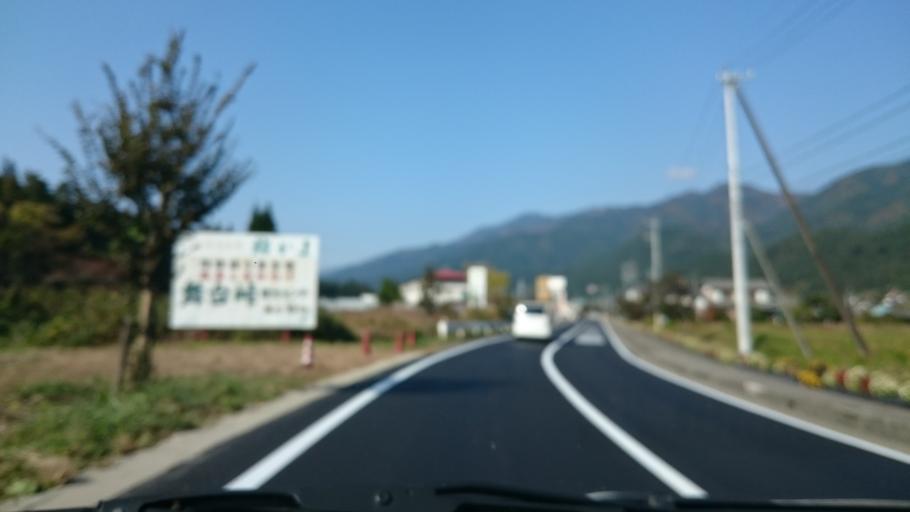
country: JP
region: Gifu
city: Nakatsugawa
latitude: 35.6943
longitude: 137.3808
